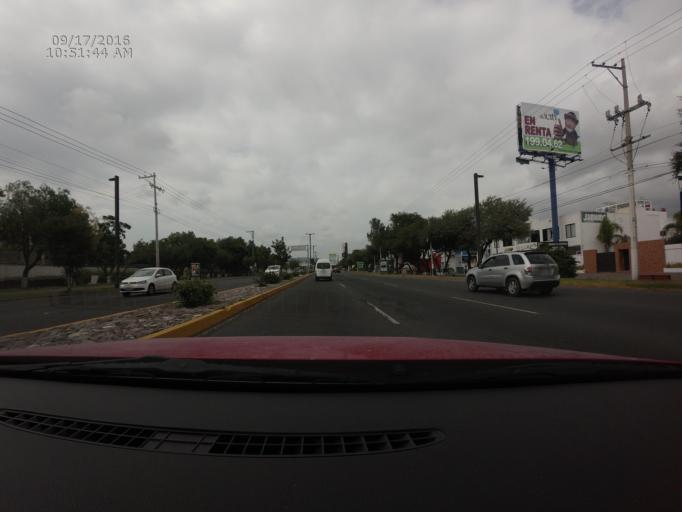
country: MX
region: Queretaro
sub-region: Corregidora
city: El Pueblito
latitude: 20.5457
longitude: -100.4281
